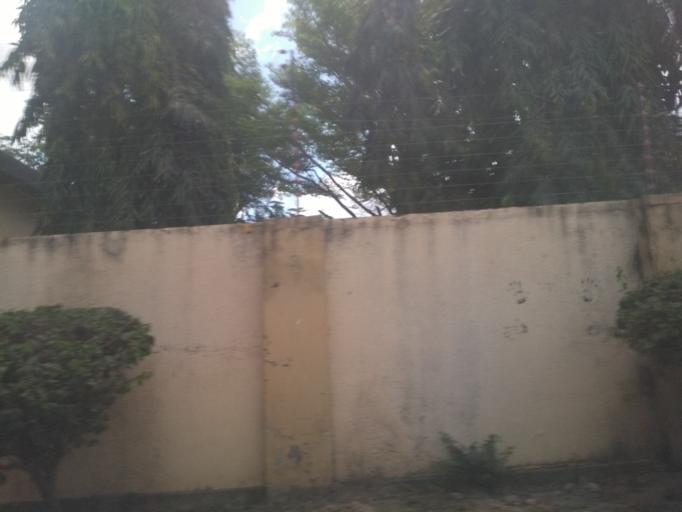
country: TZ
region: Dar es Salaam
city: Dar es Salaam
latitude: -6.8476
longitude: 39.2649
